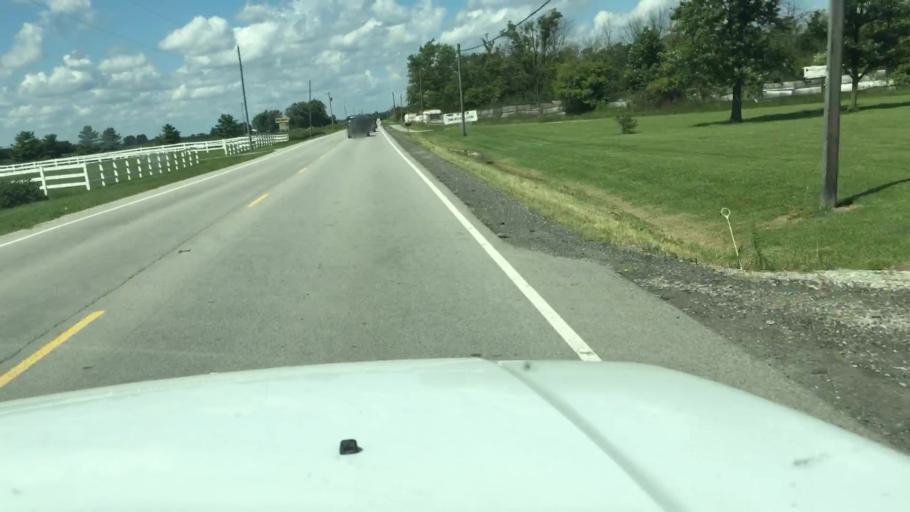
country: US
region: Ohio
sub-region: Madison County
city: Mount Sterling
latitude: 39.7440
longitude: -83.2816
